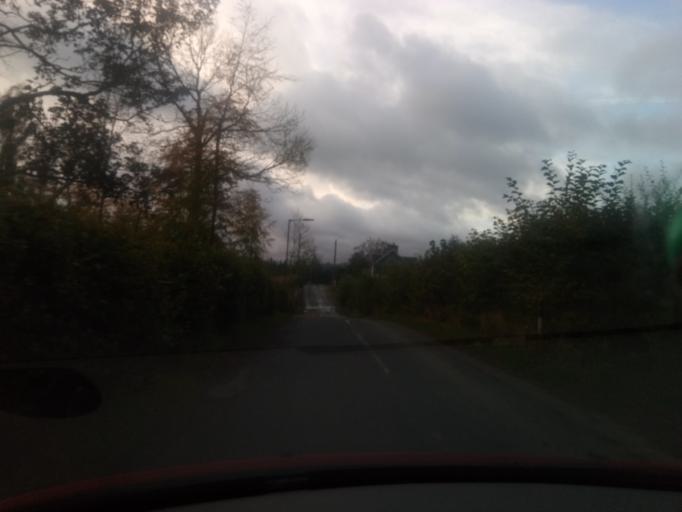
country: GB
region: Scotland
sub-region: The Scottish Borders
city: Jedburgh
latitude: 55.4045
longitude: -2.6552
